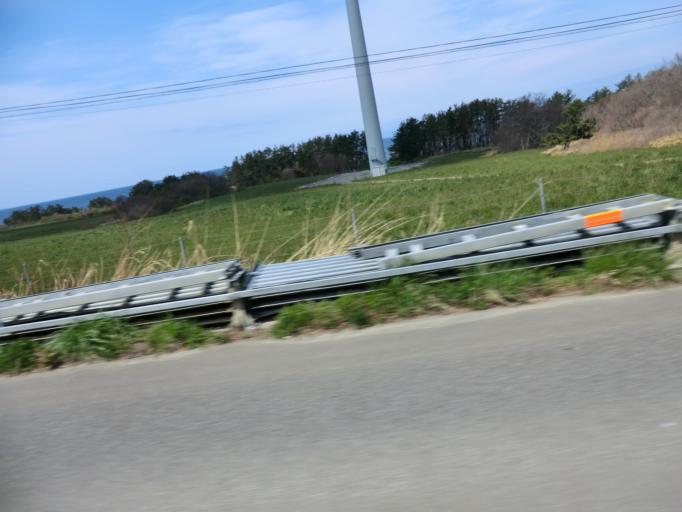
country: JP
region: Hokkaido
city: Hakodate
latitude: 41.4638
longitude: 140.8865
